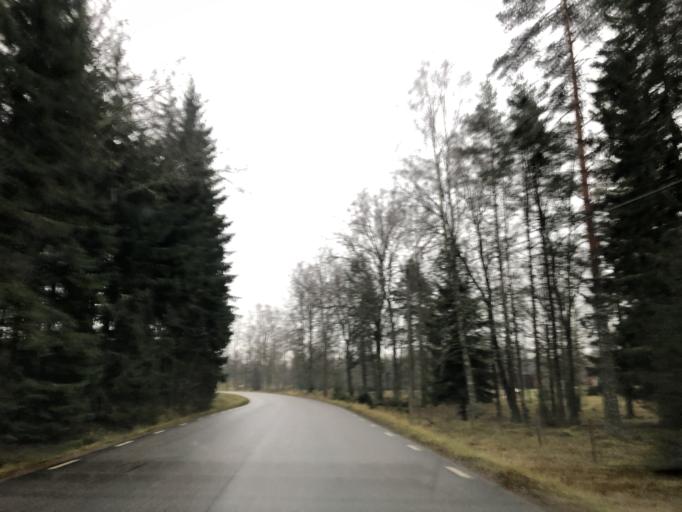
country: SE
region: Vaestra Goetaland
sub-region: Ulricehamns Kommun
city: Ulricehamn
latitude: 57.8510
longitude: 13.2570
